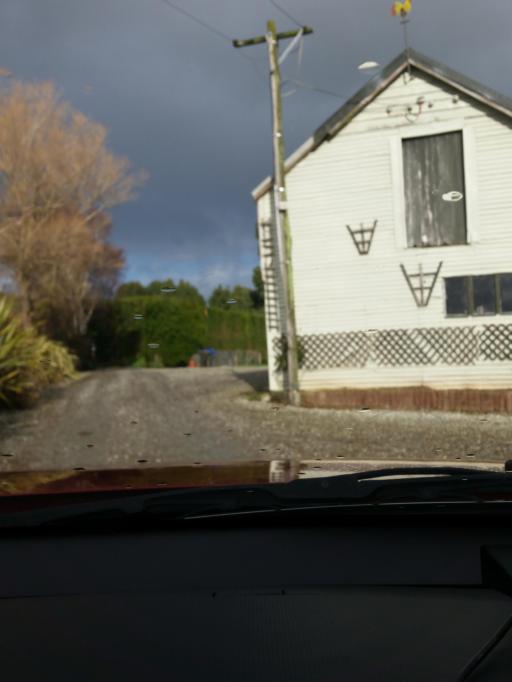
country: NZ
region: Southland
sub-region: Invercargill City
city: Invercargill
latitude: -46.3272
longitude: 168.4719
